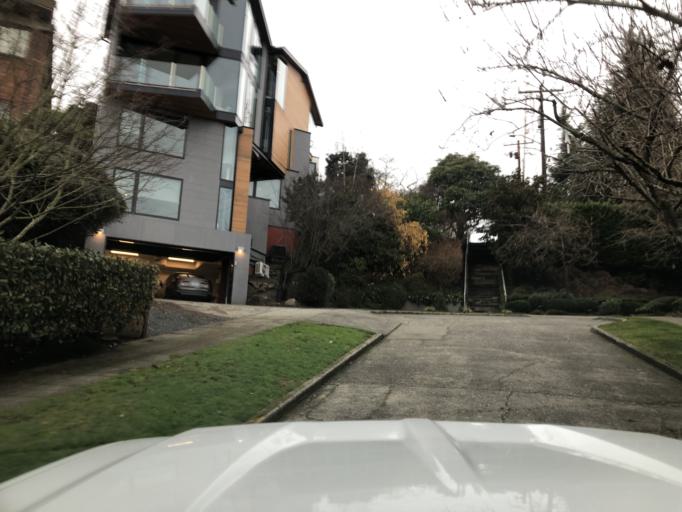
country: US
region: Washington
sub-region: King County
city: Seattle
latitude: 47.6291
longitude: -122.3514
